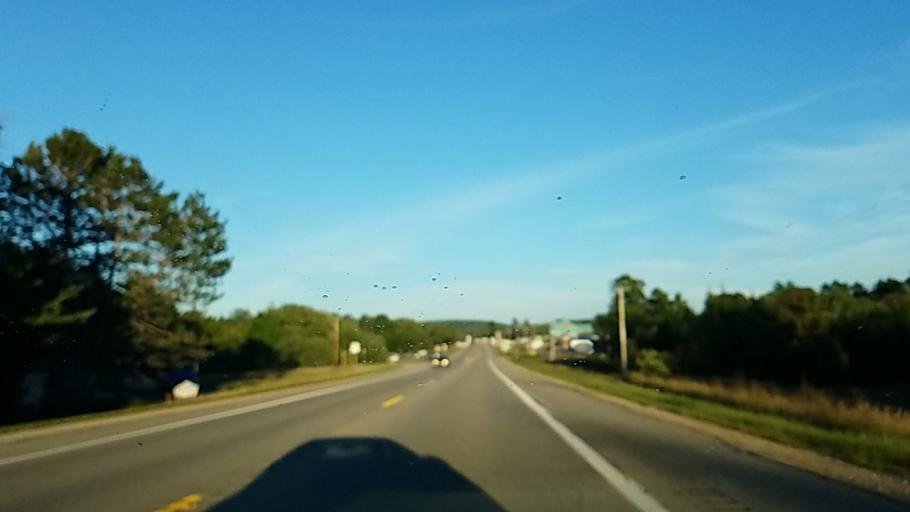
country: US
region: Michigan
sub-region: Alger County
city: Munising
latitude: 46.4389
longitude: -86.7128
